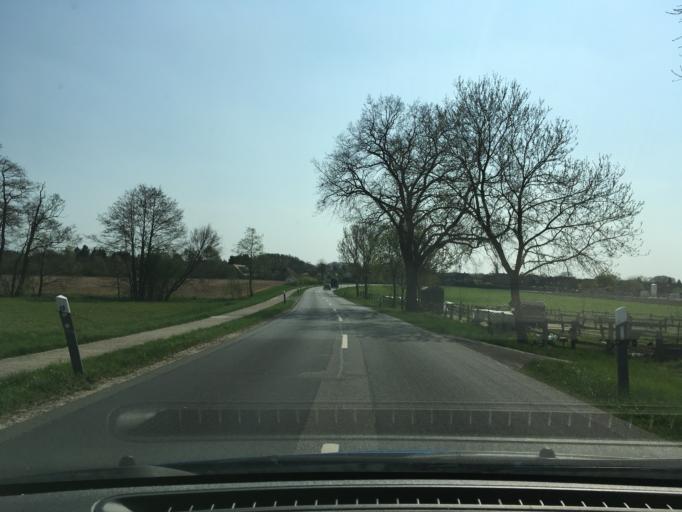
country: DE
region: Lower Saxony
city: Kirchgellersen
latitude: 53.2378
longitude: 10.2987
